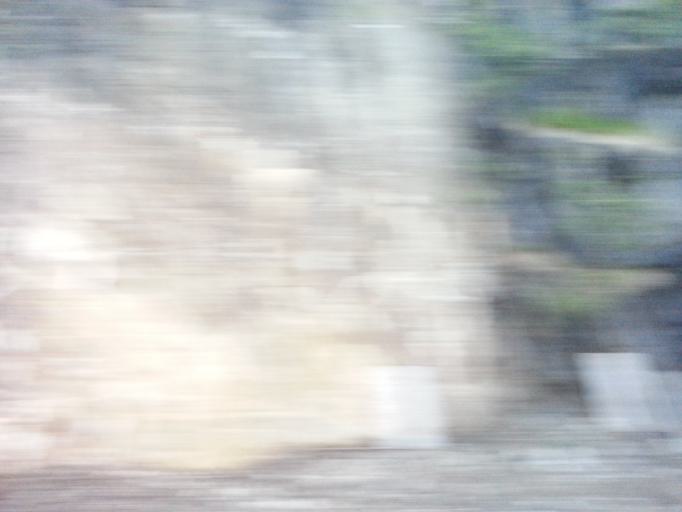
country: NO
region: Oppland
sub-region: Dovre
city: Dombas
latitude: 62.0651
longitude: 9.1241
